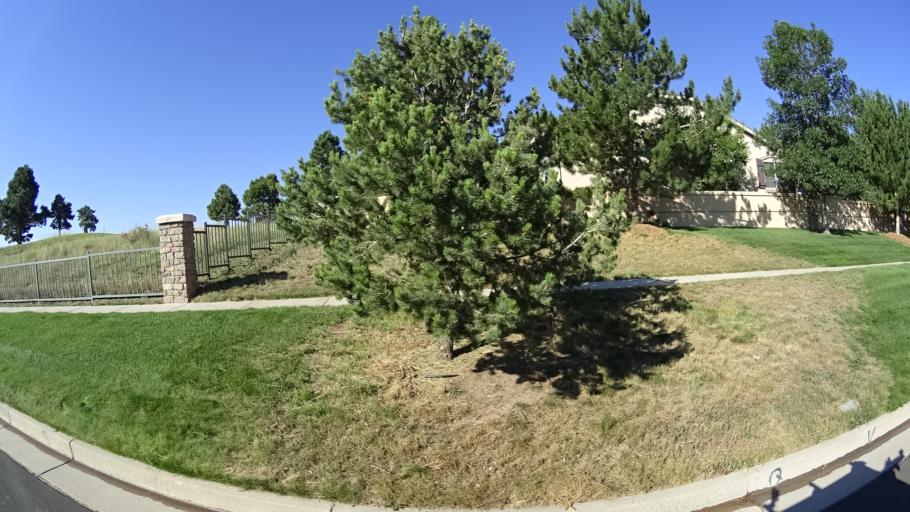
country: US
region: Colorado
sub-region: El Paso County
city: Black Forest
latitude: 38.9811
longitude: -104.7685
